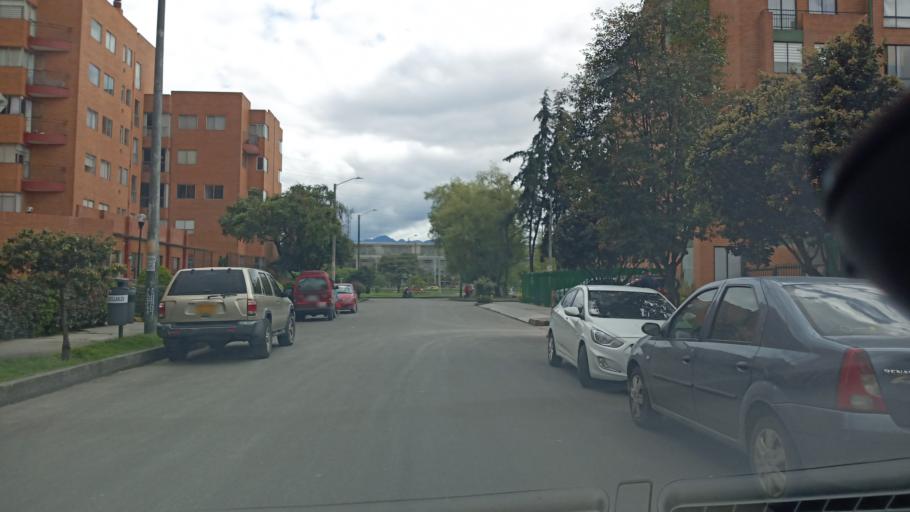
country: CO
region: Bogota D.C.
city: Bogota
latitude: 4.6662
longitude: -74.1325
